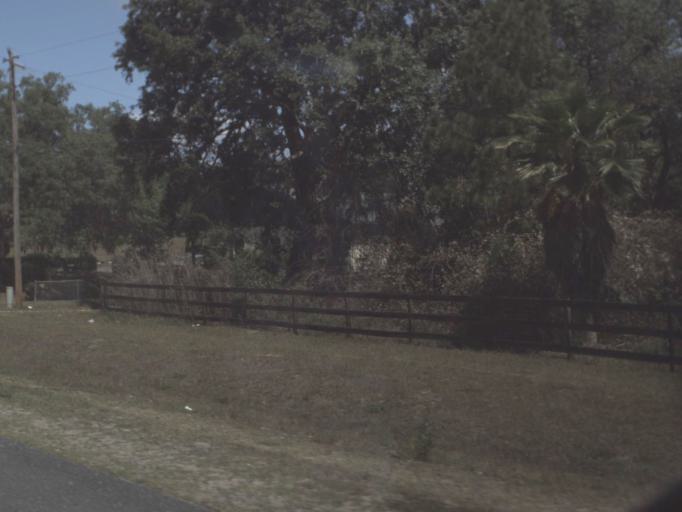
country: US
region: Florida
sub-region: Marion County
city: Silver Springs Shores
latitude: 29.1780
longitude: -81.8796
